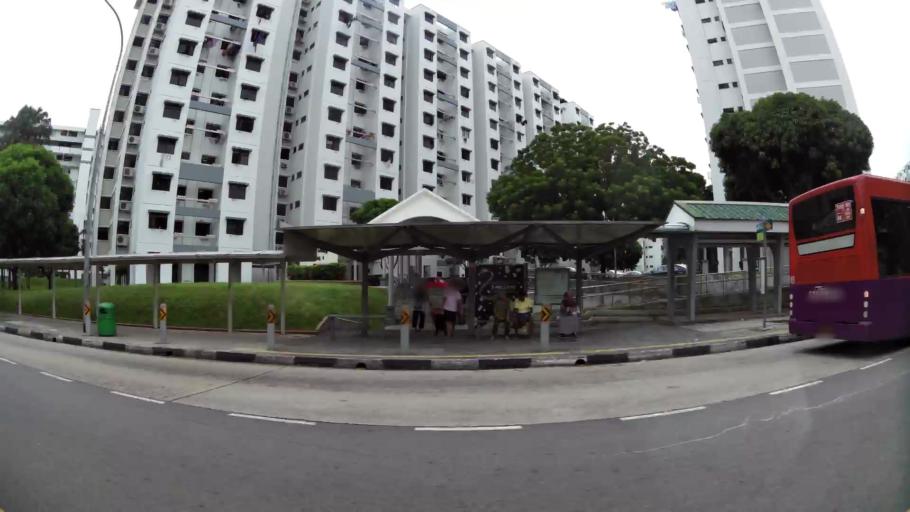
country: SG
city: Singapore
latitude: 1.3642
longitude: 103.8922
